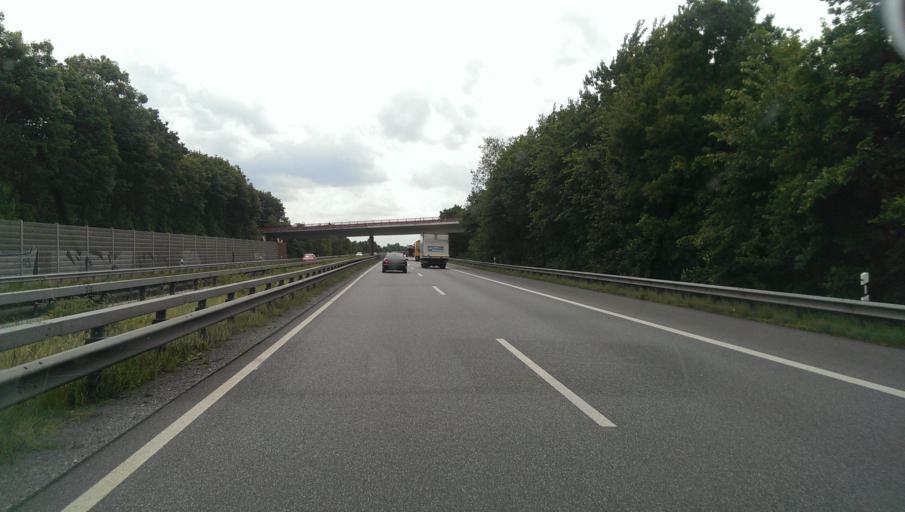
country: DE
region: Lower Saxony
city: Driftsethe
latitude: 53.4105
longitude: 8.5803
